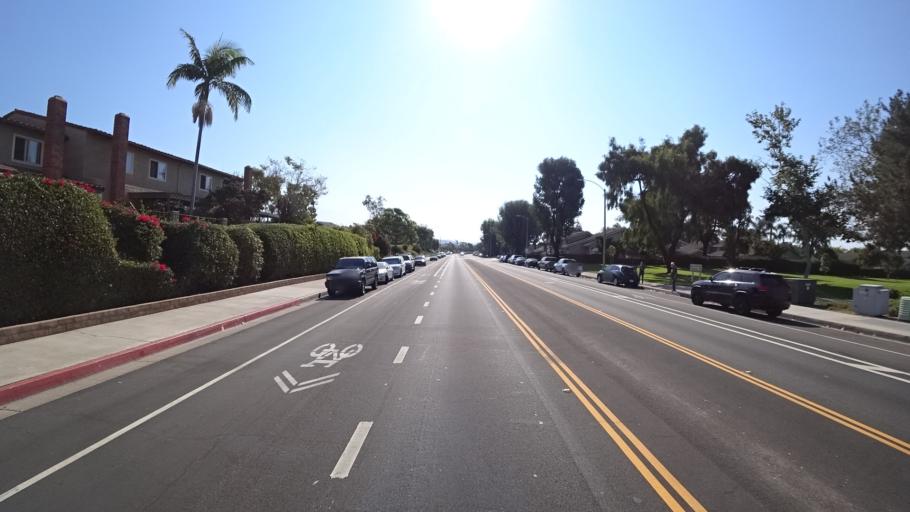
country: US
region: California
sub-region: Orange County
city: Dana Point
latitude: 33.4548
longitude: -117.6553
